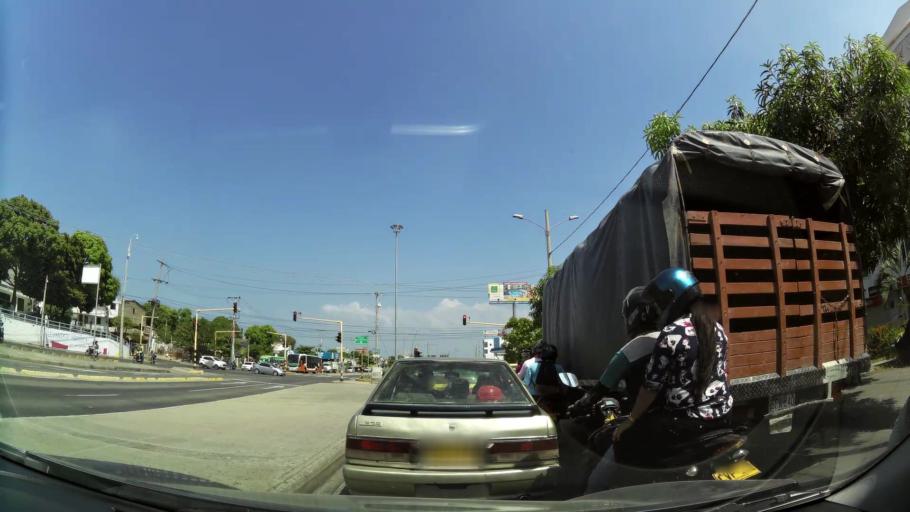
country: CO
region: Bolivar
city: Cartagena
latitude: 10.3955
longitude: -75.4773
